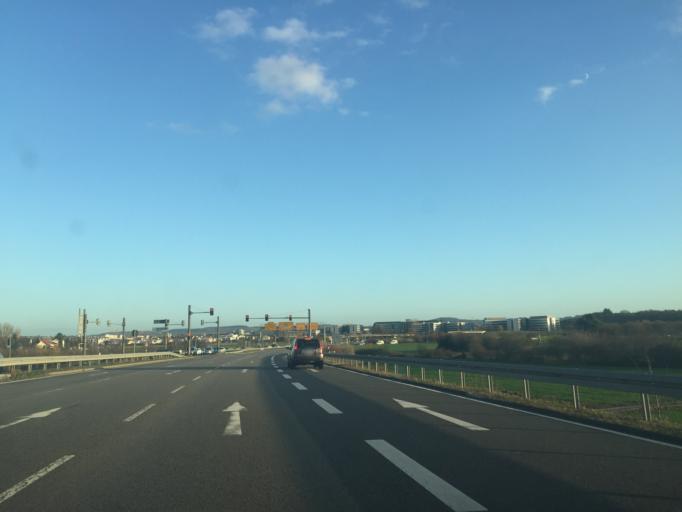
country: DE
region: Baden-Wuerttemberg
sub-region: Karlsruhe Region
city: Walldorf
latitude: 49.3010
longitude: 8.6286
